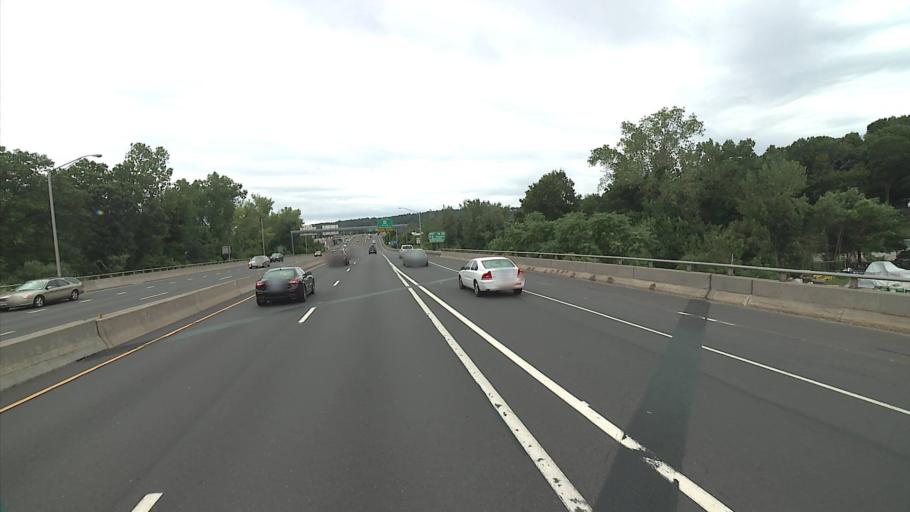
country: US
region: Connecticut
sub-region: New Haven County
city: Derby
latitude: 41.3248
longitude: -73.0852
